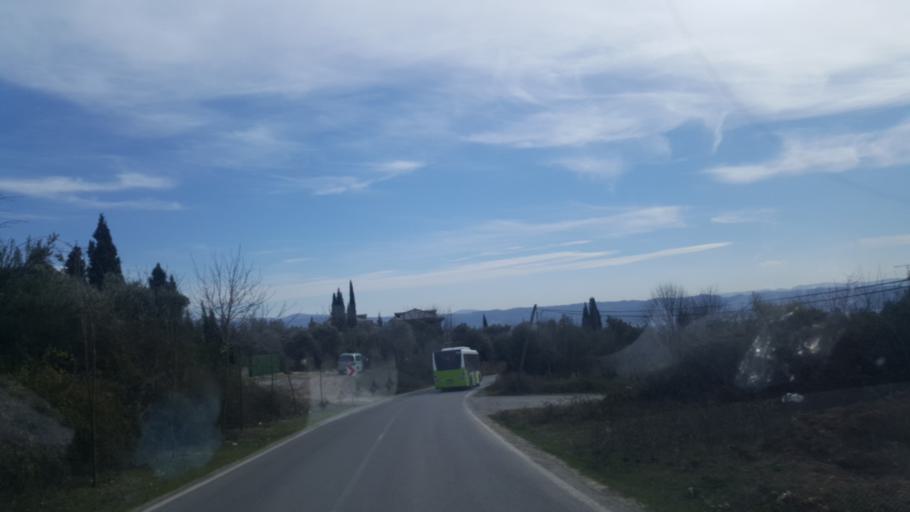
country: TR
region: Kocaeli
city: Tavsancil
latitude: 40.7803
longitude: 29.5750
